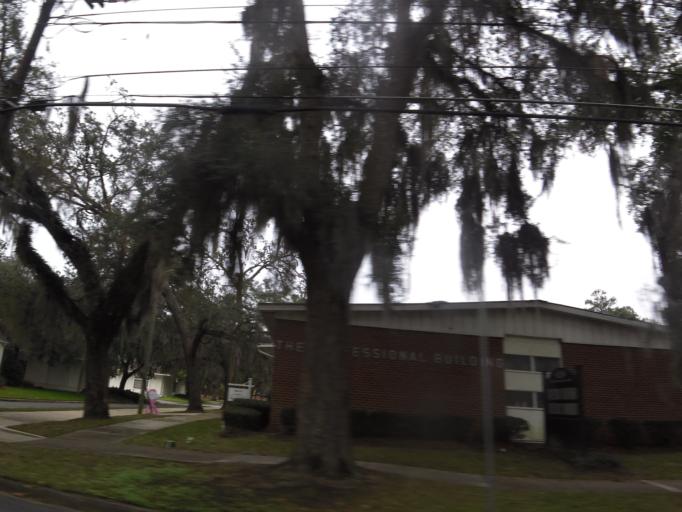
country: US
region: Georgia
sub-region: Thomas County
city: Thomasville
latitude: 30.8310
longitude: -83.9760
